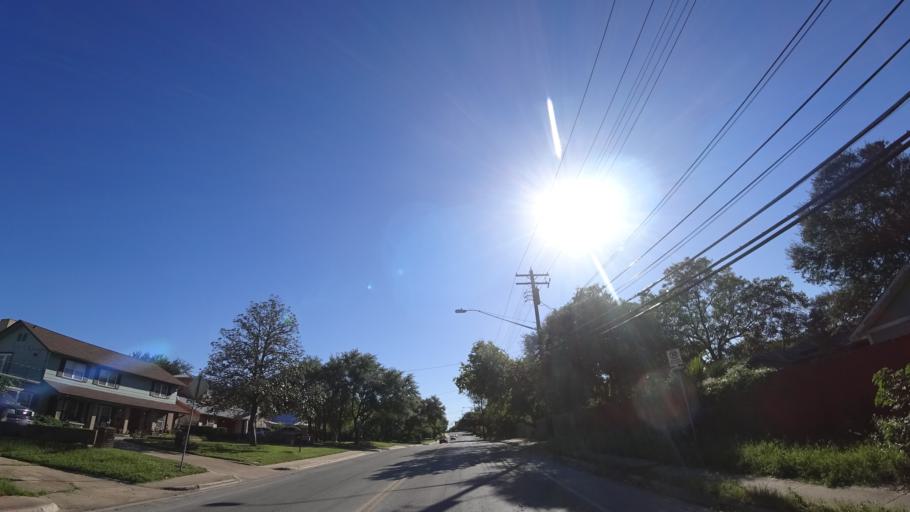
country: US
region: Texas
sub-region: Travis County
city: Austin
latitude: 30.2373
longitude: -97.7336
